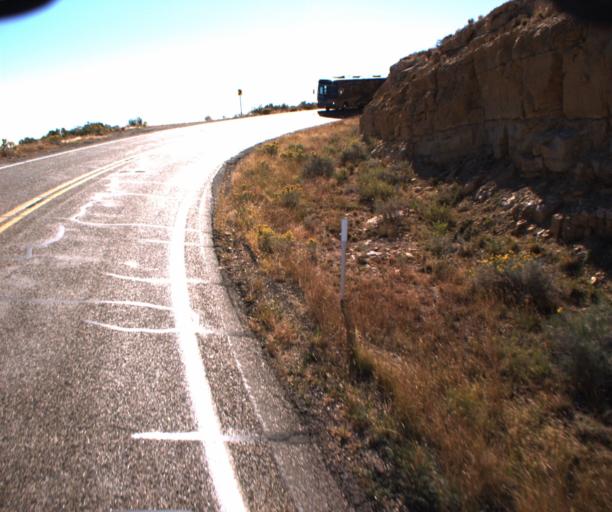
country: US
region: Arizona
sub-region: Coconino County
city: Fredonia
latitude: 36.7327
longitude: -112.0595
